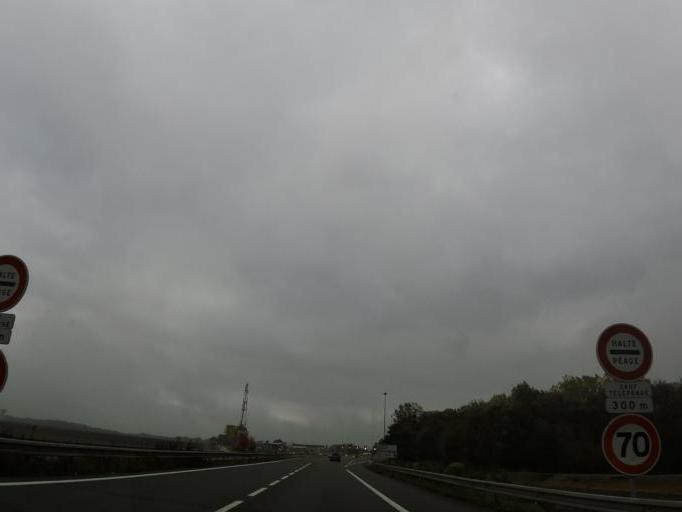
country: FR
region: Ile-de-France
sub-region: Departement de Seine-et-Marne
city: Chamigny
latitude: 49.0076
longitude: 3.1416
